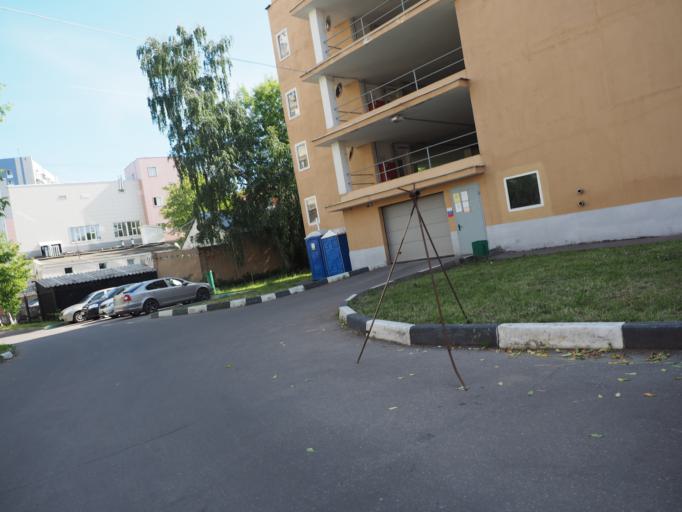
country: RU
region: Moscow
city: Lefortovo
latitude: 55.7777
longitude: 37.7274
